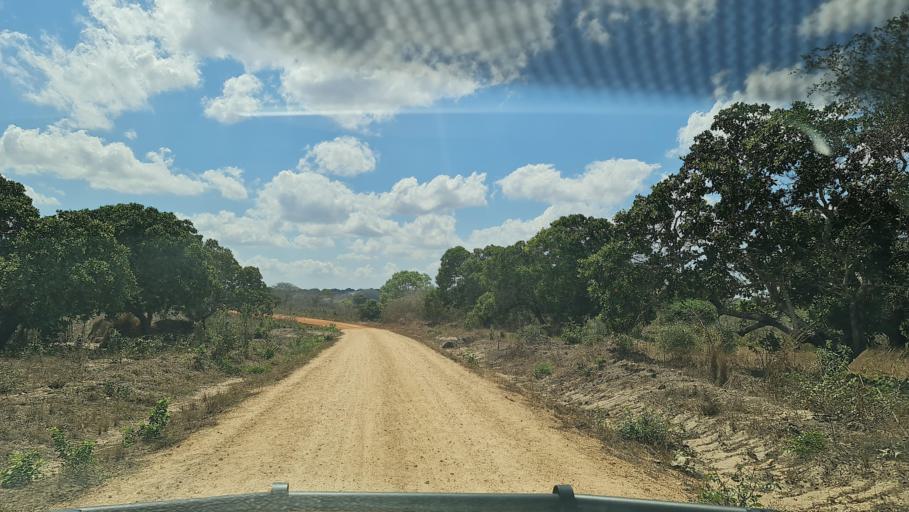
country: MZ
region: Nampula
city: Nacala
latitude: -14.1737
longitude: 40.2404
